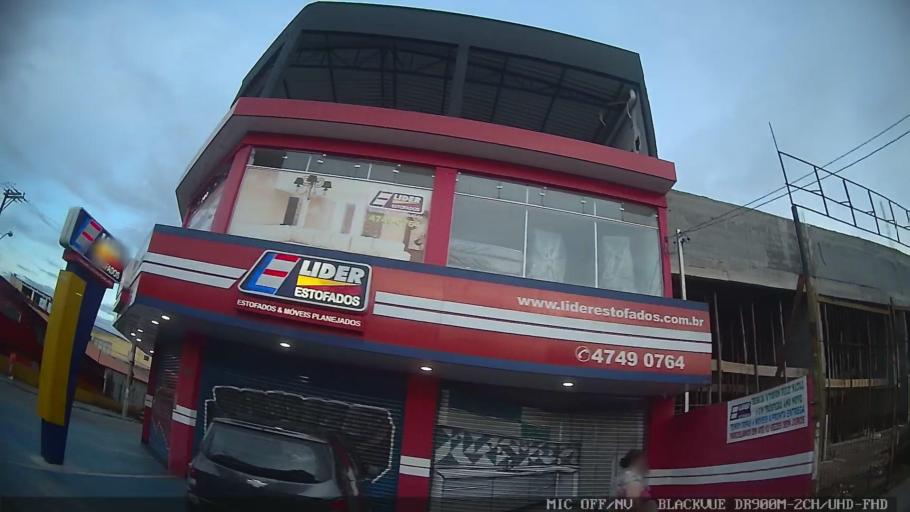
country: BR
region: Sao Paulo
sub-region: Itaquaquecetuba
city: Itaquaquecetuba
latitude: -23.4972
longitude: -46.3162
